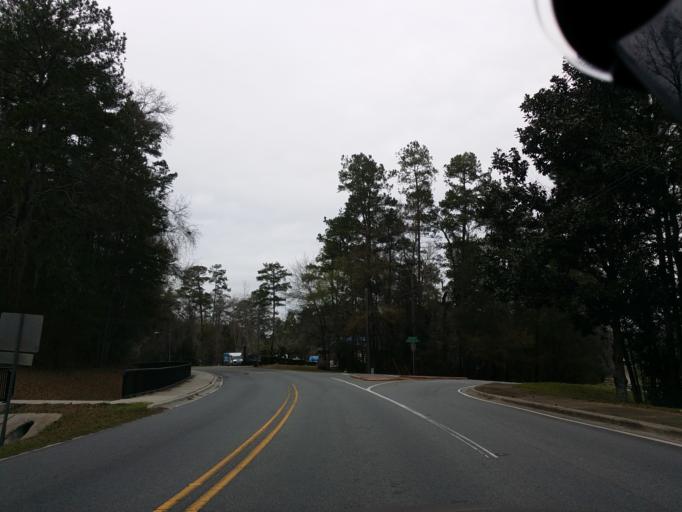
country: US
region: Florida
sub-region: Leon County
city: Tallahassee
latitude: 30.4842
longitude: -84.2269
